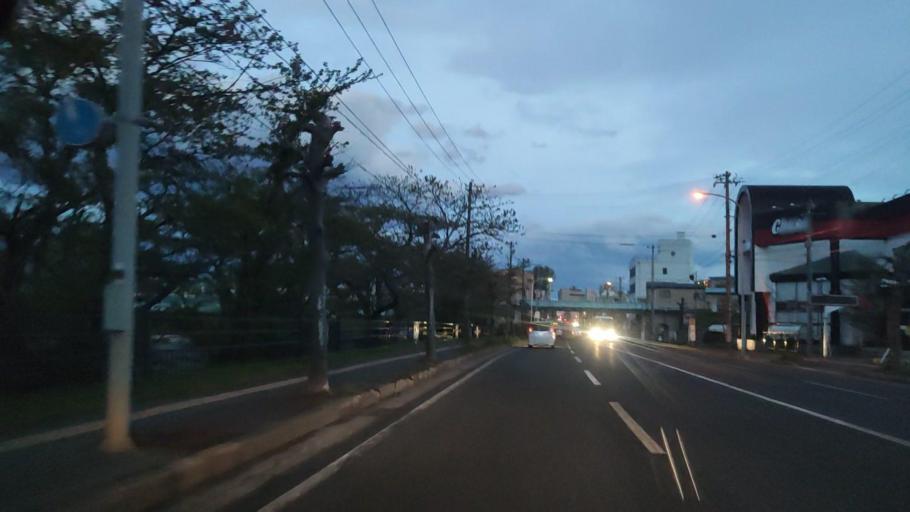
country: JP
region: Iwate
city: Morioka-shi
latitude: 39.7117
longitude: 141.1316
